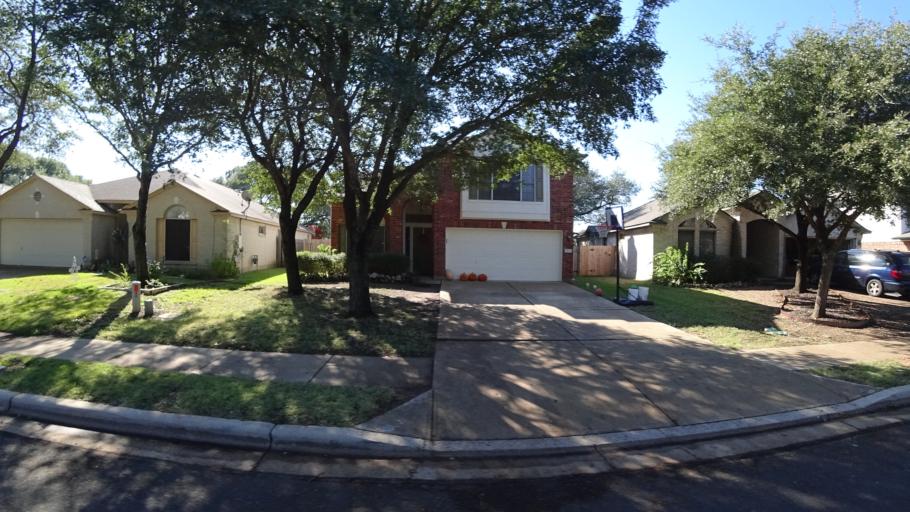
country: US
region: Texas
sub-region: Travis County
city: Shady Hollow
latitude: 30.1945
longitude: -97.8585
